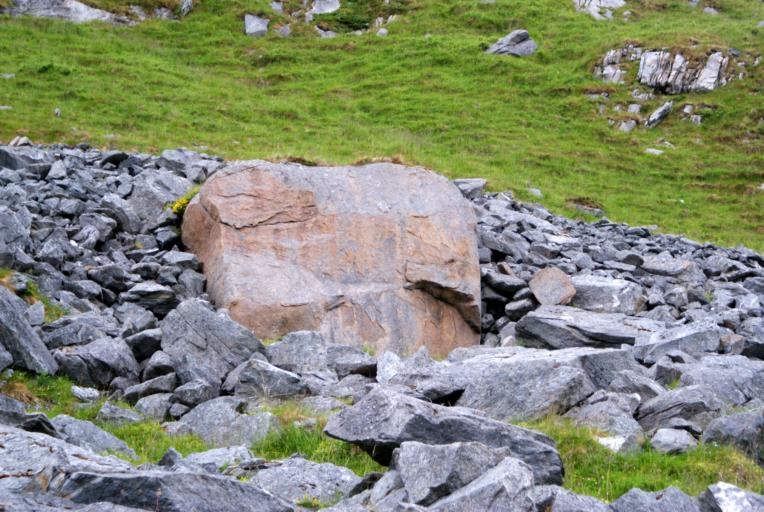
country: NO
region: Nordland
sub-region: Vestvagoy
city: Gravdal
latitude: 68.1994
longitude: 13.5145
